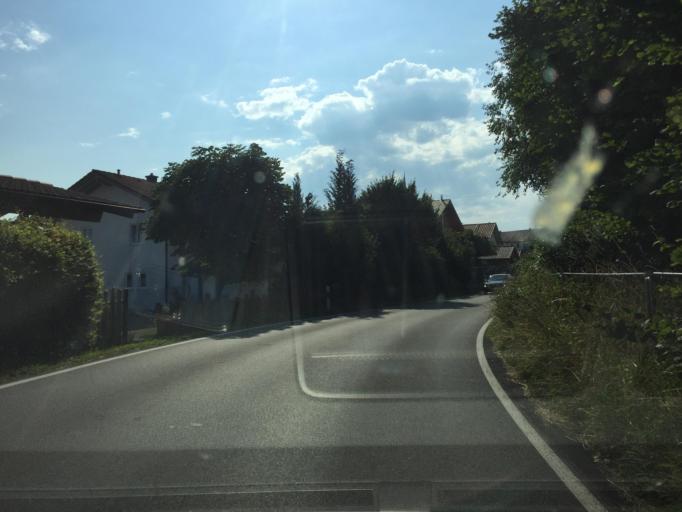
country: DE
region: Bavaria
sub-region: Upper Bavaria
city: Tuntenhausen
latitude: 47.9511
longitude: 12.0308
